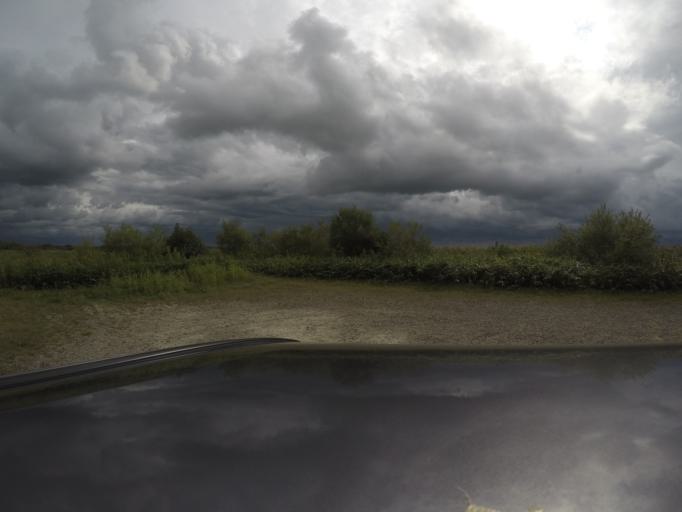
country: JP
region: Hokkaido
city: Makubetsu
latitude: 45.0095
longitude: 141.7321
